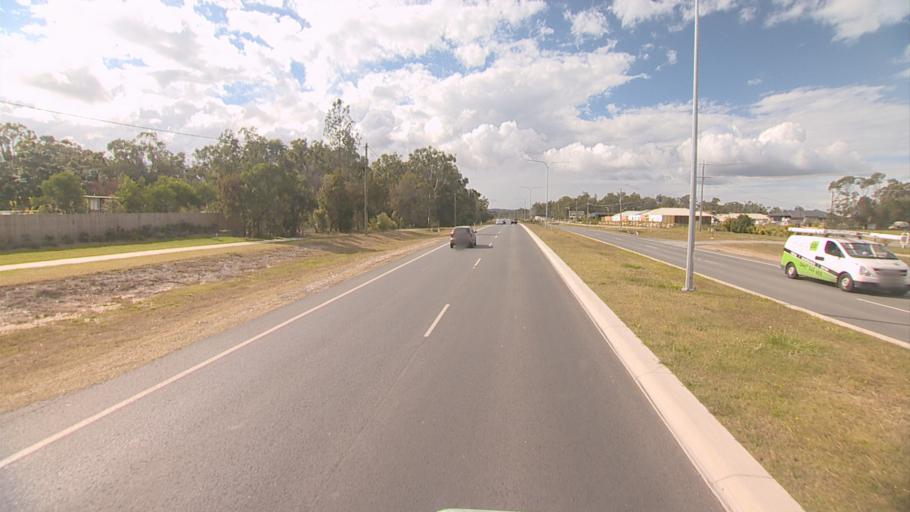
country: AU
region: Queensland
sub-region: Logan
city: Logan Reserve
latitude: -27.7054
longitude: 153.0951
